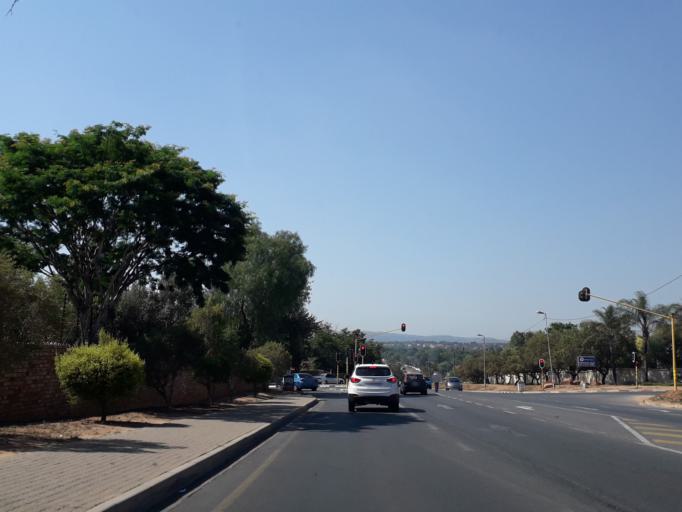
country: ZA
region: Gauteng
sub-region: City of Johannesburg Metropolitan Municipality
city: Diepsloot
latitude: -26.0572
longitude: 27.9702
